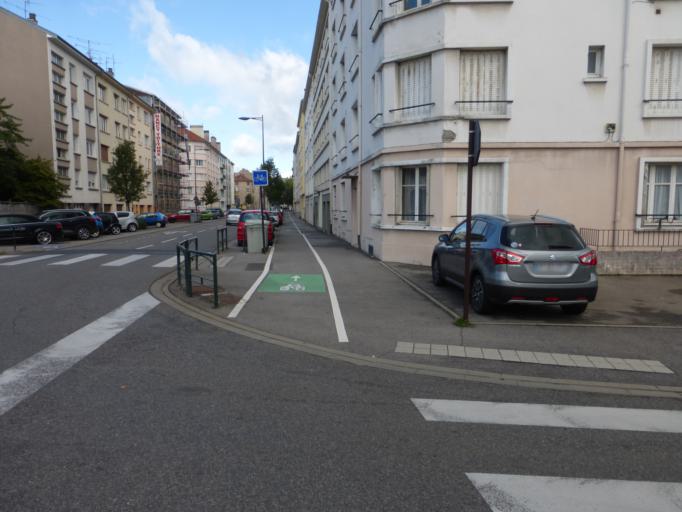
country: FR
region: Lorraine
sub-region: Departement de Meurthe-et-Moselle
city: Villers-les-Nancy
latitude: 48.6766
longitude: 6.1611
